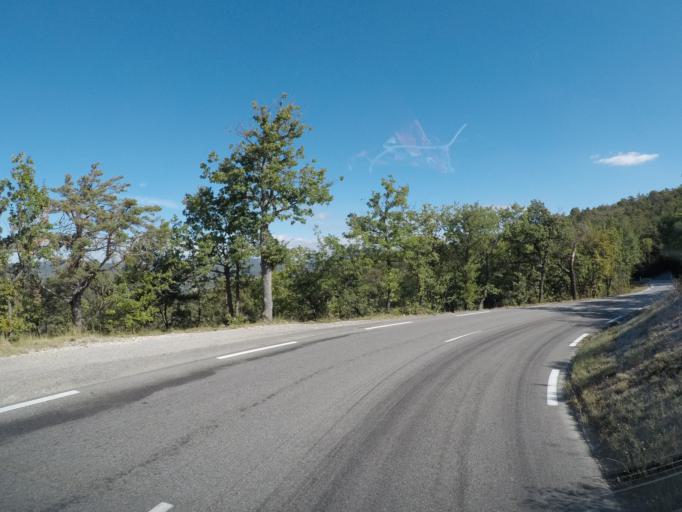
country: FR
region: Provence-Alpes-Cote d'Azur
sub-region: Departement des Alpes-de-Haute-Provence
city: Riez
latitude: 43.9012
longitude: 6.1389
